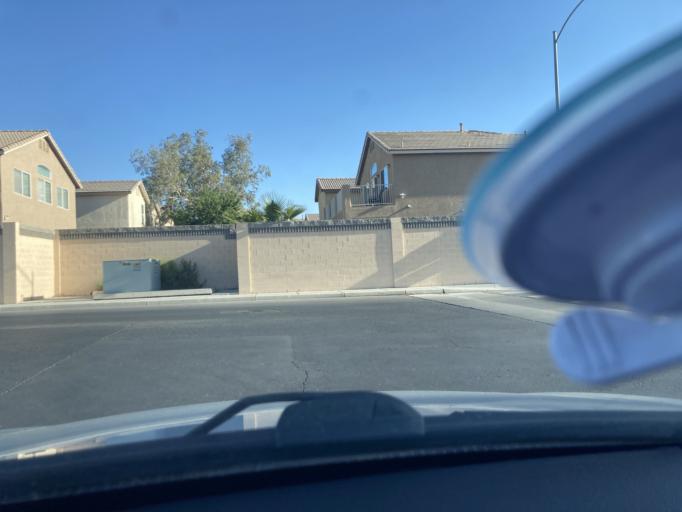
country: US
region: Nevada
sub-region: Clark County
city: Enterprise
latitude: 36.0593
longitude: -115.2929
